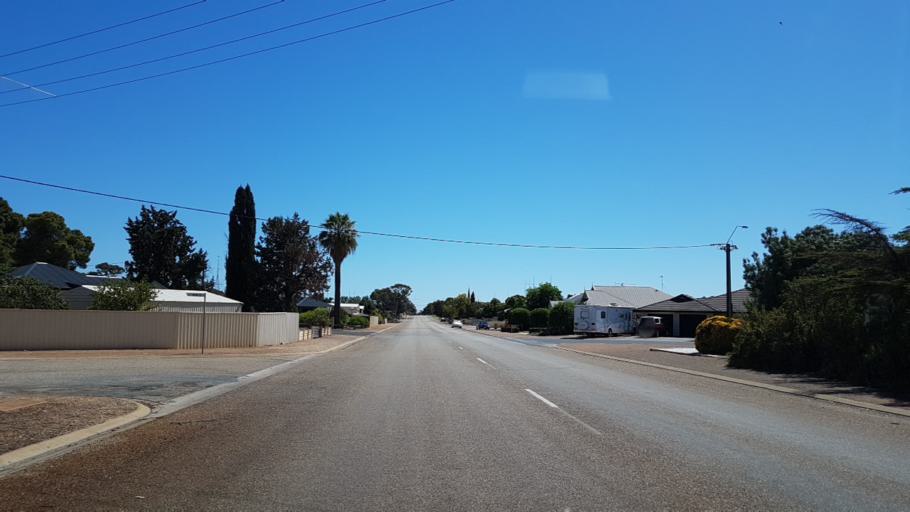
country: AU
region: South Australia
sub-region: Copper Coast
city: Kadina
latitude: -33.9654
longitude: 137.7231
